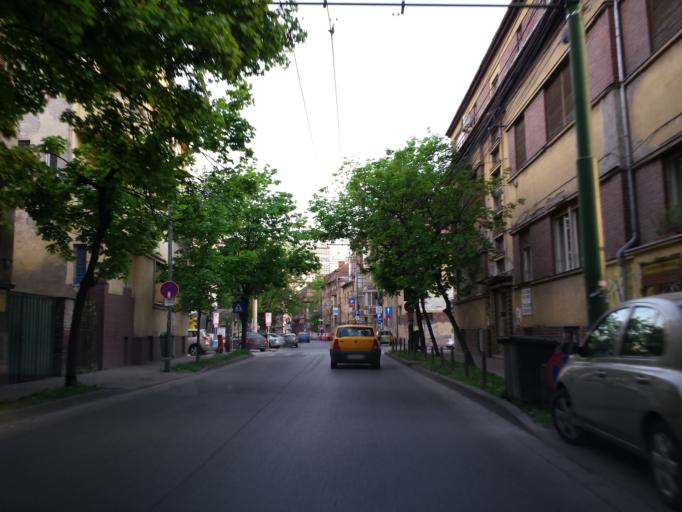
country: RO
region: Timis
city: Timisoara
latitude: 45.7556
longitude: 21.2231
